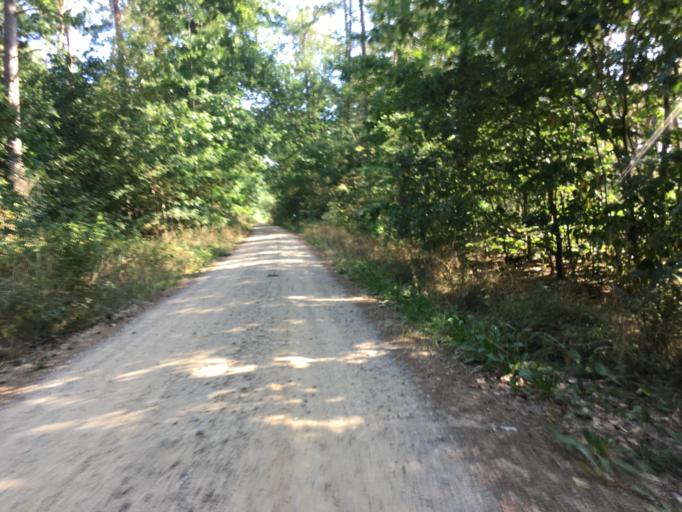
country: DE
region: Brandenburg
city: Liebenwalde
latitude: 52.9163
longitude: 13.4297
